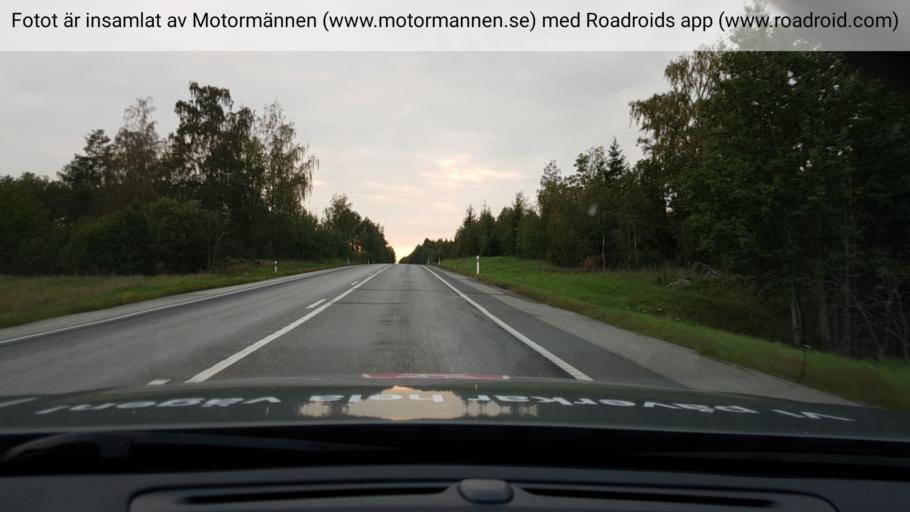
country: SE
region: OErebro
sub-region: Lindesbergs Kommun
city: Fellingsbro
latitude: 59.3429
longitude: 15.5767
